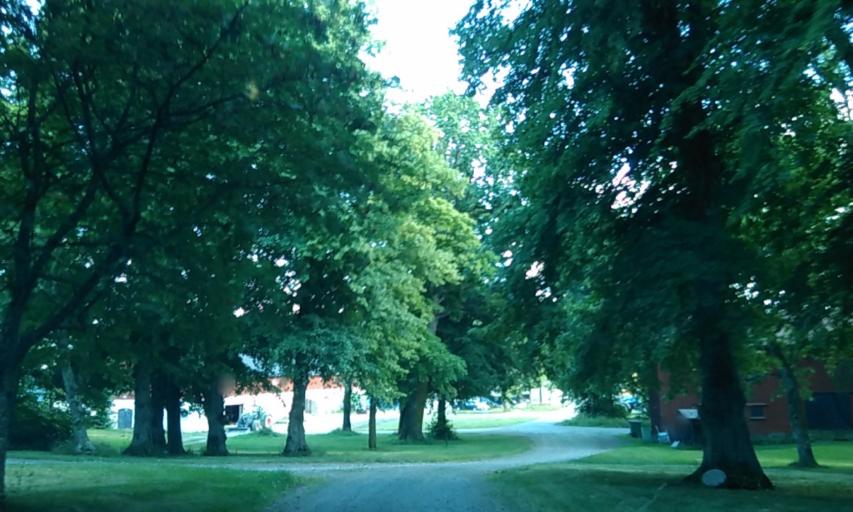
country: SE
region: Vaestra Goetaland
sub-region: Lidkopings Kommun
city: Lidkoping
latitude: 58.5797
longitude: 13.0113
